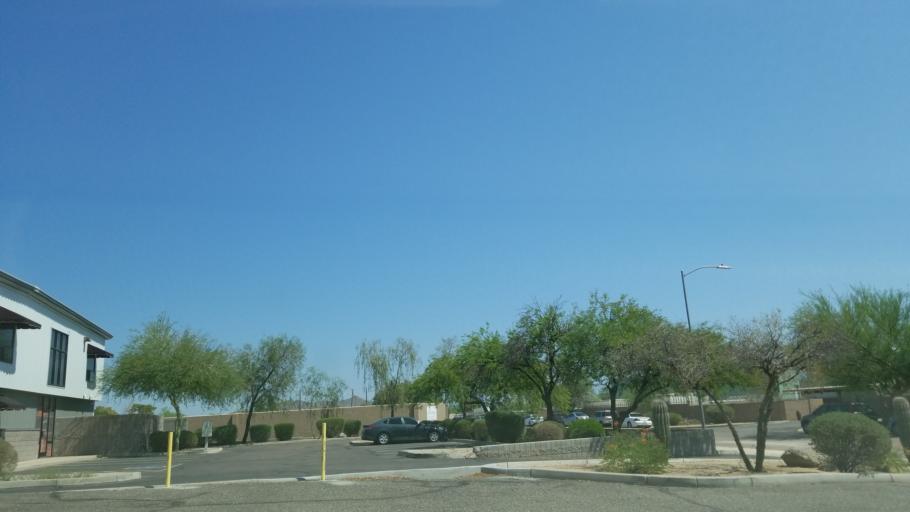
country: US
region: Arizona
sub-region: Maricopa County
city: Paradise Valley
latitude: 33.6771
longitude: -112.0351
